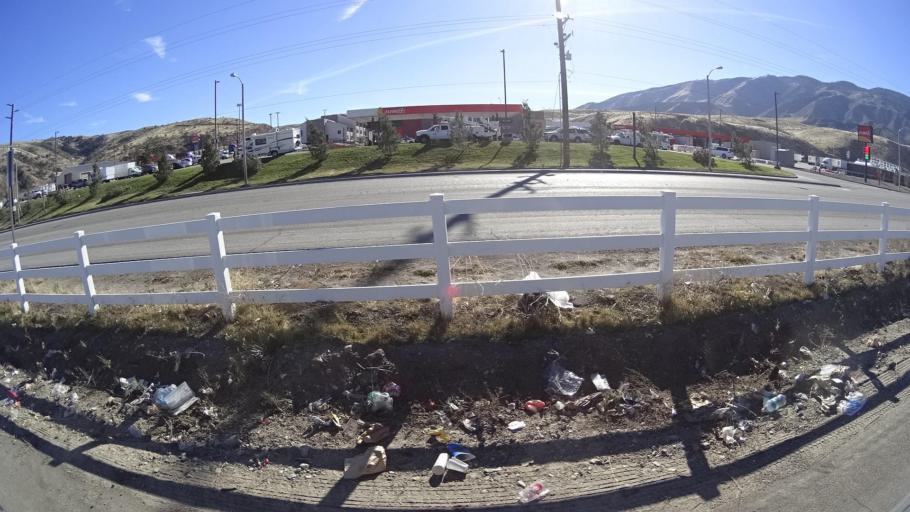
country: US
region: California
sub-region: Kern County
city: Lebec
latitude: 34.8185
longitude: -118.8876
